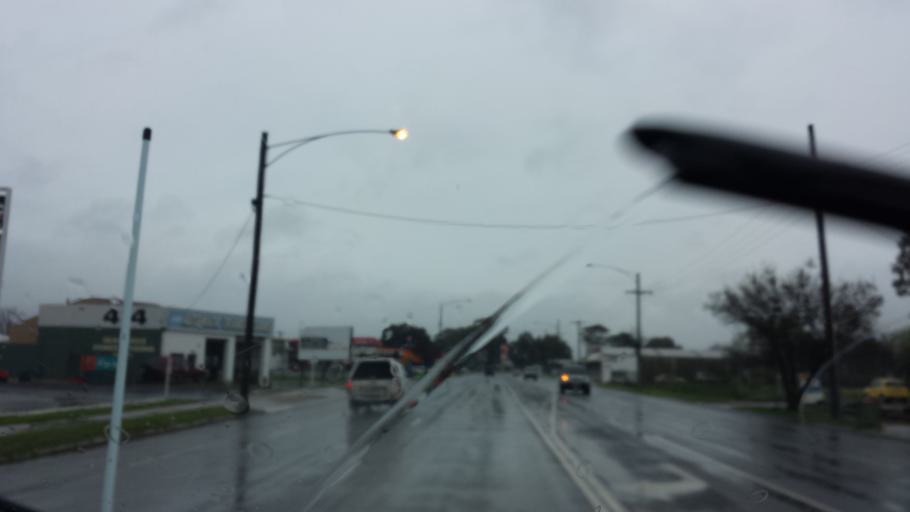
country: AU
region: Victoria
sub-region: Benalla
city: Benalla
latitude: -36.5494
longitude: 145.9938
